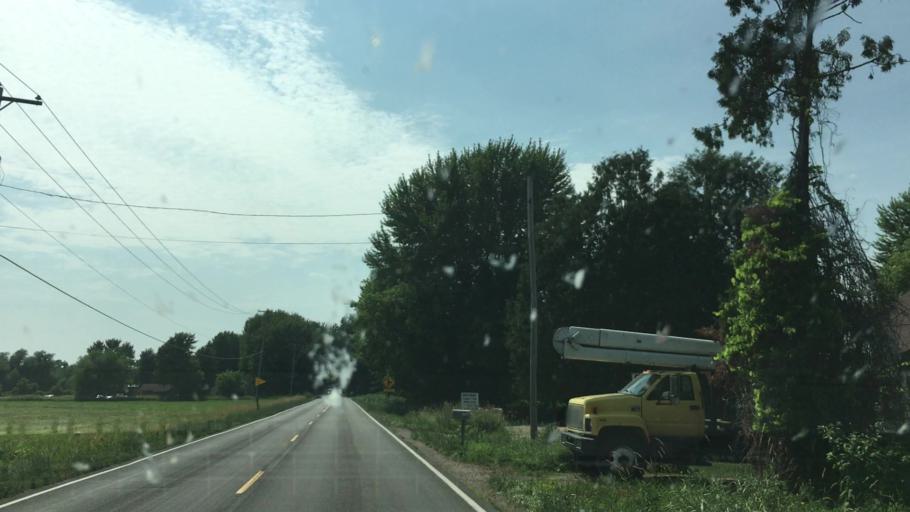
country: US
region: Michigan
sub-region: Kent County
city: Byron Center
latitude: 42.7829
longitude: -85.7103
